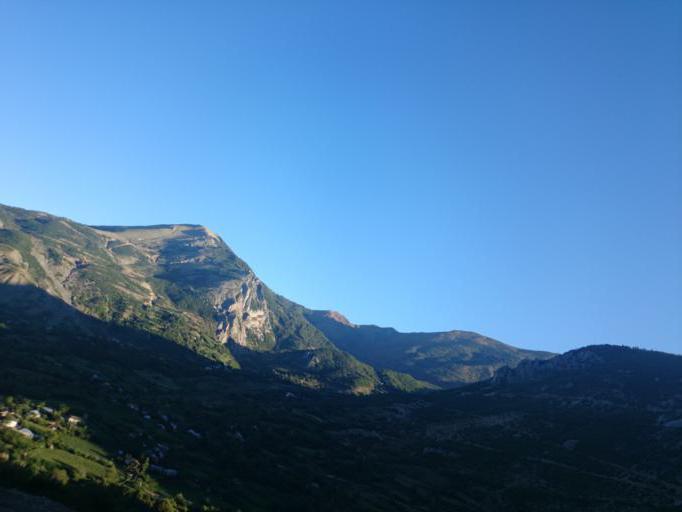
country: AL
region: Elbasan
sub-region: Rrethi i Gramshit
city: Kukur
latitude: 40.8623
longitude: 20.3688
